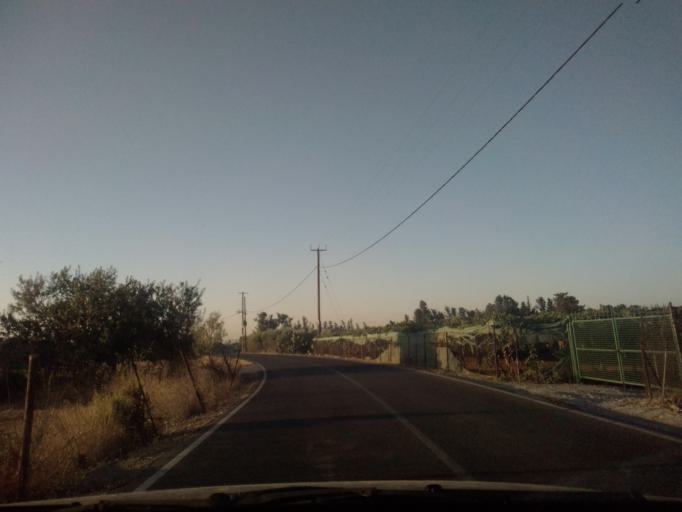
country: CY
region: Limassol
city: Ypsonas
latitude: 34.6719
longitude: 32.9590
